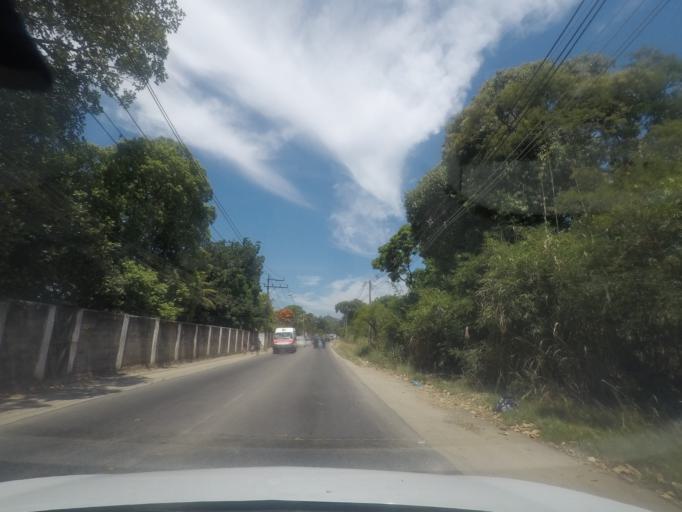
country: BR
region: Rio de Janeiro
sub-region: Itaguai
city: Itaguai
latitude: -22.9846
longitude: -43.6584
